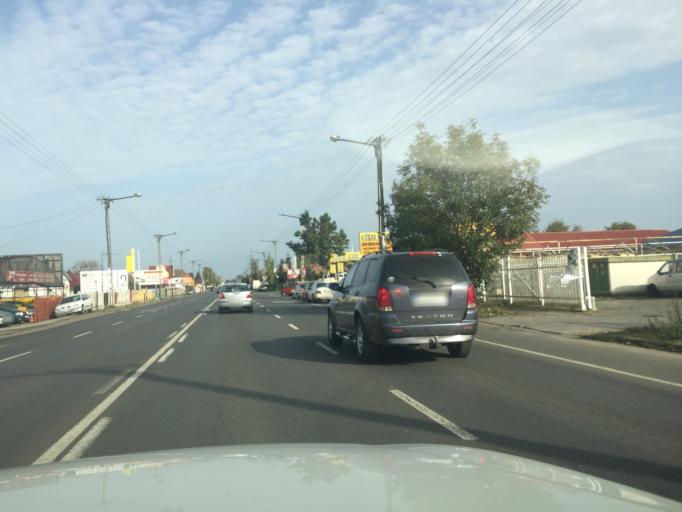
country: HU
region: Szabolcs-Szatmar-Bereg
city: Nyiregyhaza
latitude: 47.9279
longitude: 21.7187
